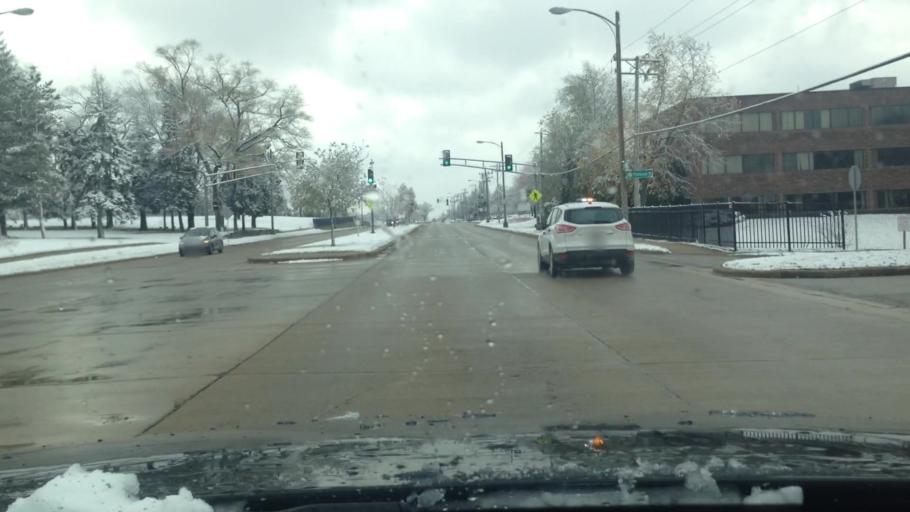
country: US
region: Illinois
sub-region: DuPage County
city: Lombard
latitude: 41.8527
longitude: -88.0267
